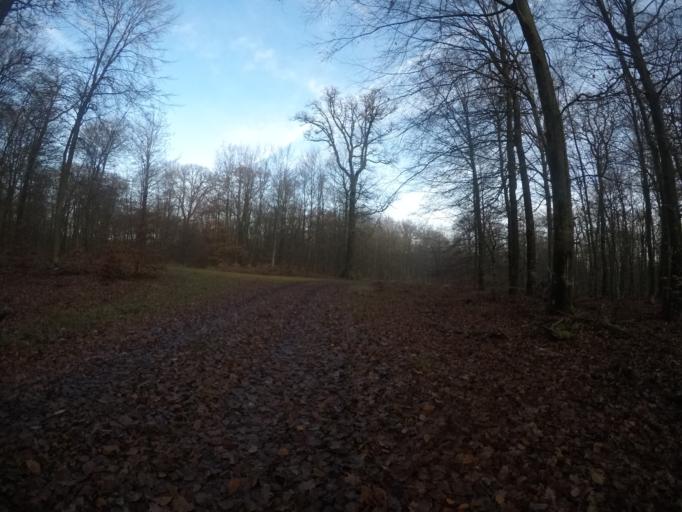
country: BE
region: Wallonia
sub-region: Province du Luxembourg
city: Habay-la-Vieille
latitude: 49.7560
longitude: 5.6691
